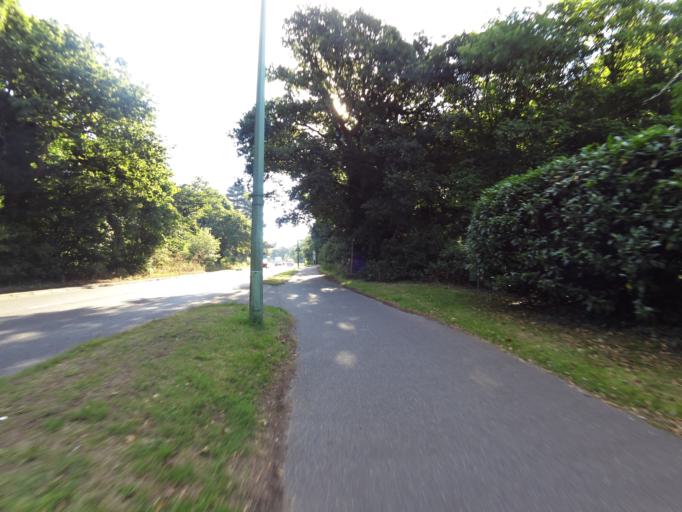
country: GB
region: England
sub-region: Suffolk
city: Kesgrave
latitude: 52.0681
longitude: 1.2630
